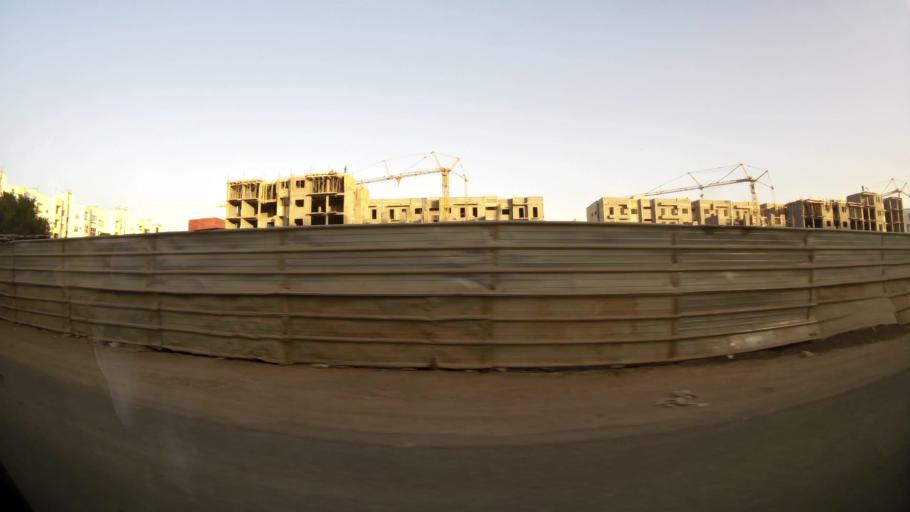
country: MA
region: Oued ed Dahab-Lagouira
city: Dakhla
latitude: 30.3975
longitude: -9.5526
